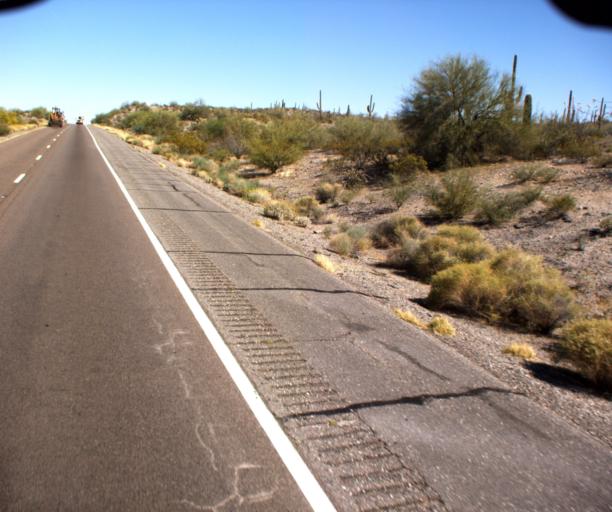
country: US
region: Arizona
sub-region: Pinal County
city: Maricopa
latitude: 32.8497
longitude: -112.3402
